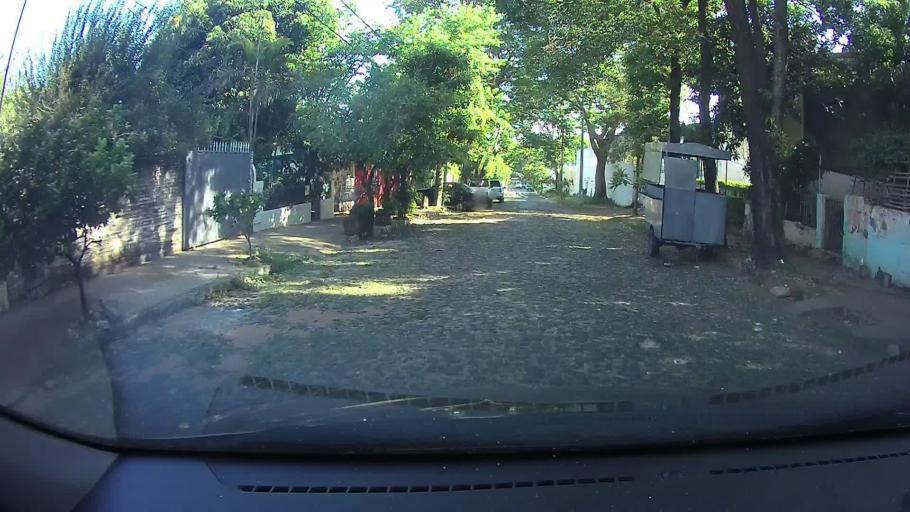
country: PY
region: Asuncion
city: Asuncion
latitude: -25.2801
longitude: -57.5986
